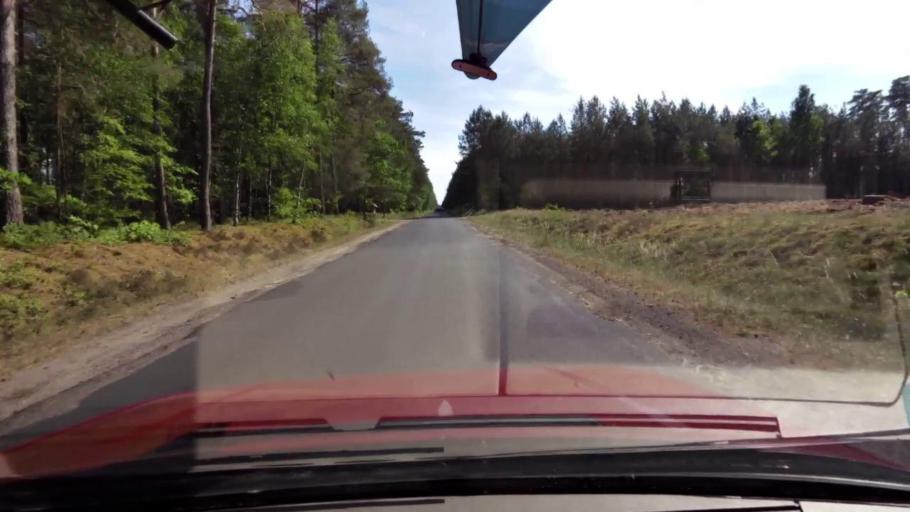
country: PL
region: Pomeranian Voivodeship
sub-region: Powiat slupski
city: Kepice
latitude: 54.3075
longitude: 16.9623
